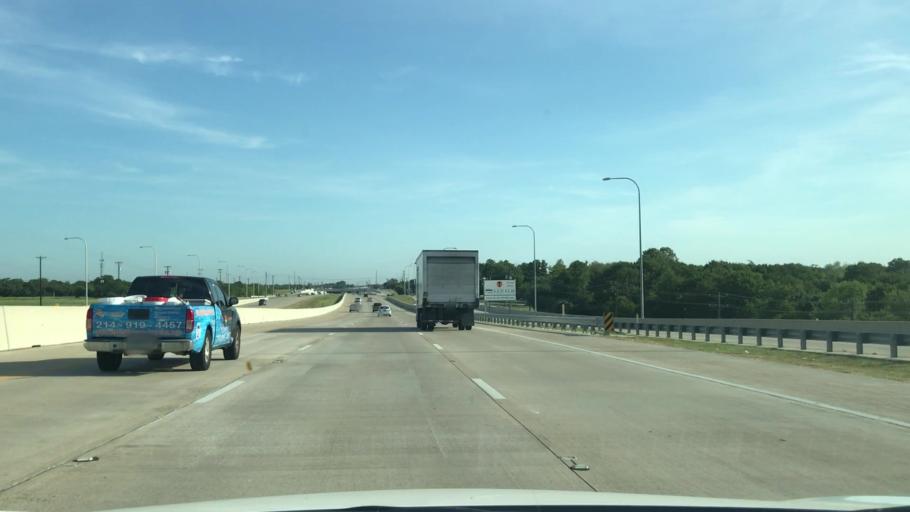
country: US
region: Texas
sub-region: Dallas County
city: Rowlett
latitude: 32.8932
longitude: -96.5560
